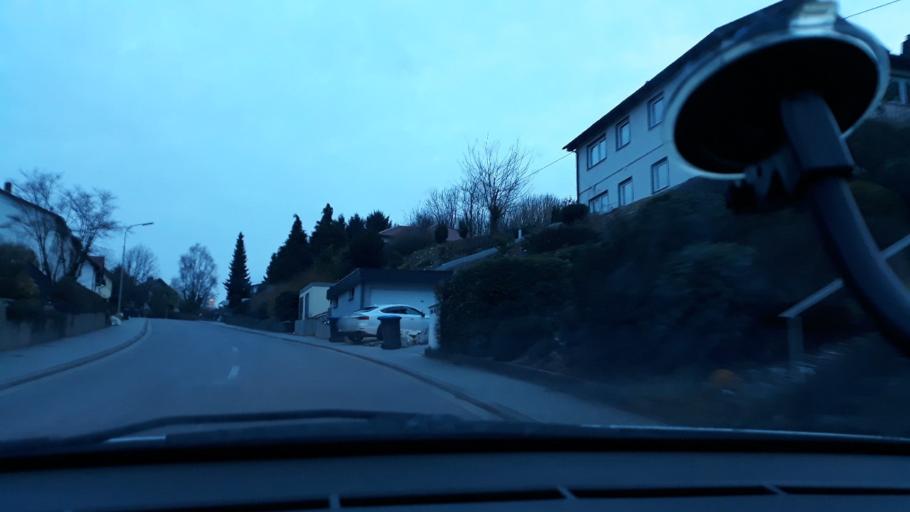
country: DE
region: Saarland
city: Gersheim
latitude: 49.2145
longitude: 7.1601
